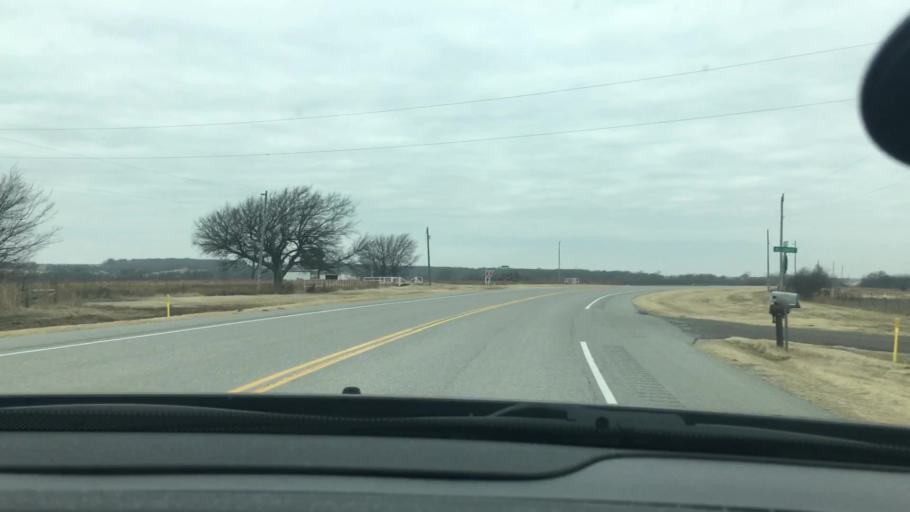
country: US
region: Oklahoma
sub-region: Murray County
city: Davis
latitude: 34.4936
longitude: -97.3693
